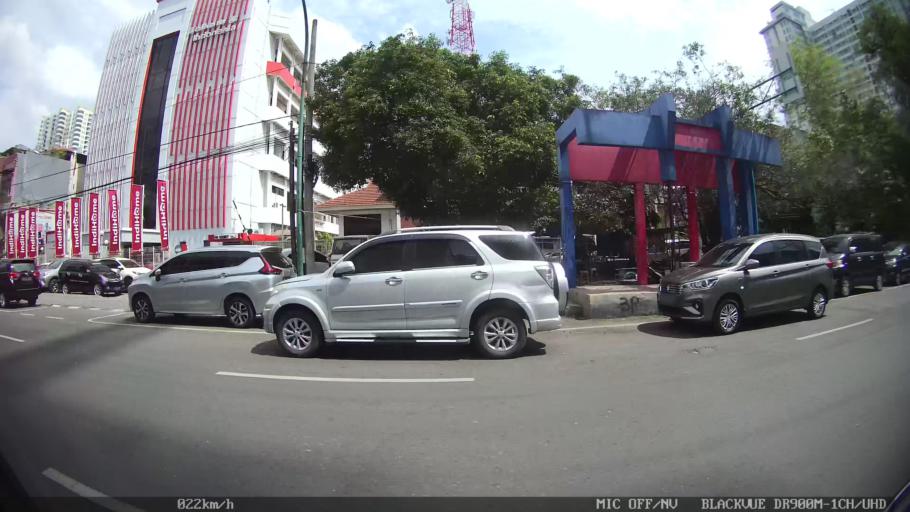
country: ID
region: North Sumatra
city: Medan
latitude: 3.5926
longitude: 98.6775
